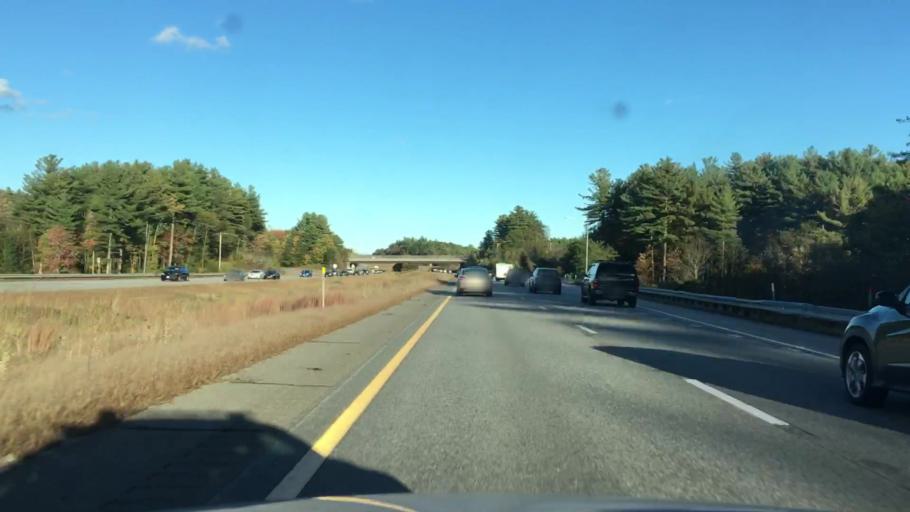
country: US
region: New Hampshire
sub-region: Rockingham County
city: Raymond
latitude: 43.0234
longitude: -71.2019
